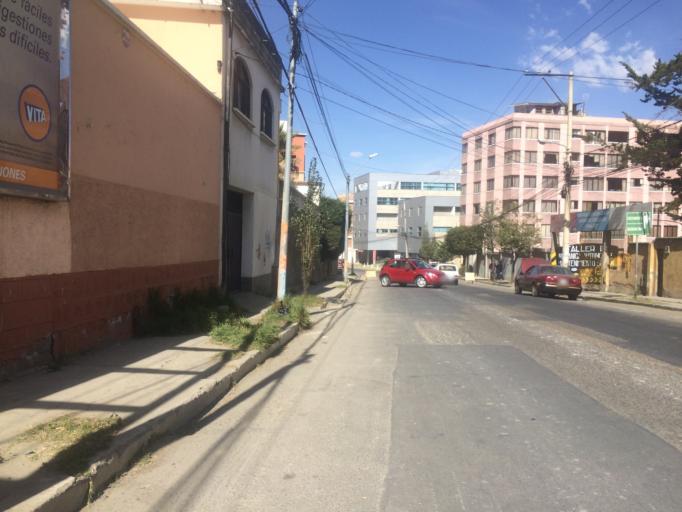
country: BO
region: La Paz
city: La Paz
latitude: -16.5238
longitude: -68.1137
